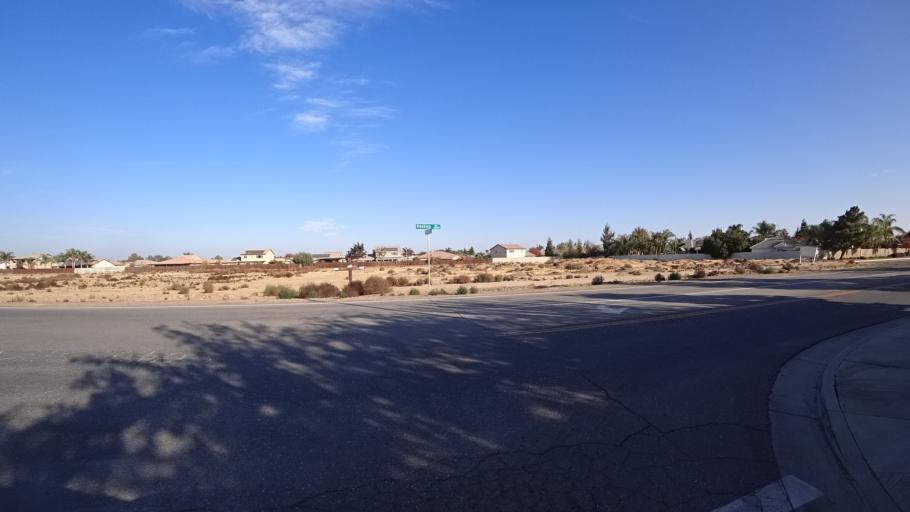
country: US
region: California
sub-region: Kern County
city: Greenfield
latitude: 35.2813
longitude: -119.0531
